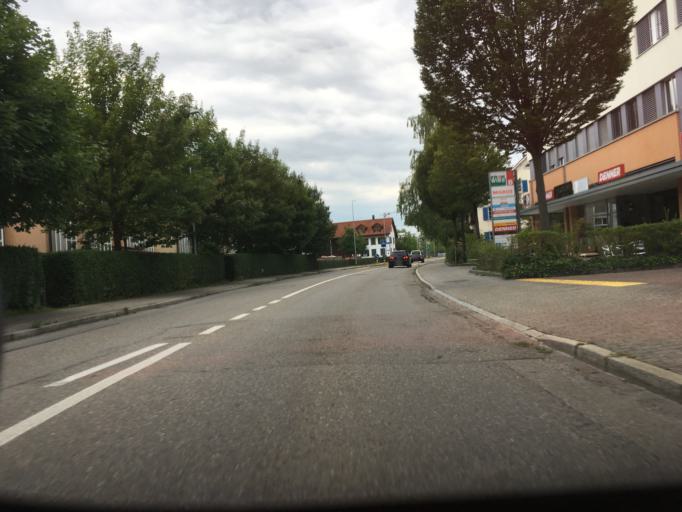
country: CH
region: Zurich
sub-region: Bezirk Pfaeffikon
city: Pfaeffikon / Pfaeffikon (Dorfkern)
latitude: 47.3678
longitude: 8.7808
